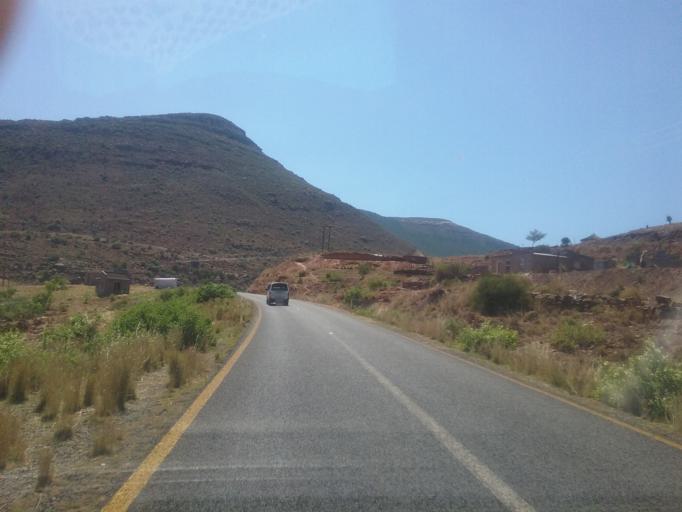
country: LS
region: Quthing
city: Quthing
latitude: -30.3666
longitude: 27.7217
